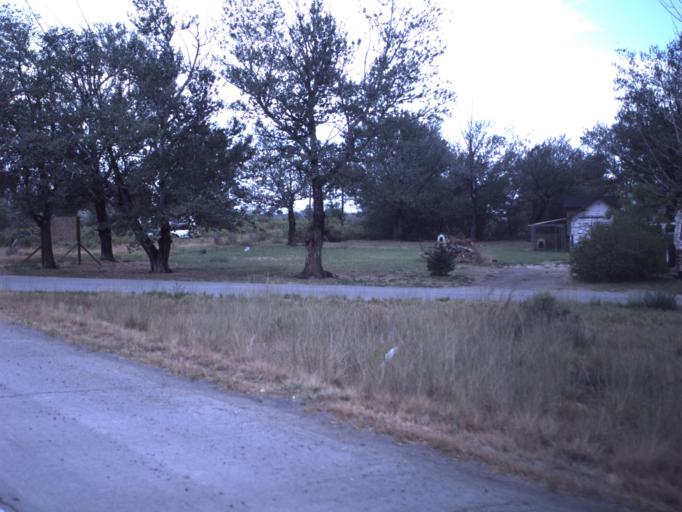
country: US
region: Utah
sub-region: Duchesne County
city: Roosevelt
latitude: 40.1966
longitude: -110.0699
